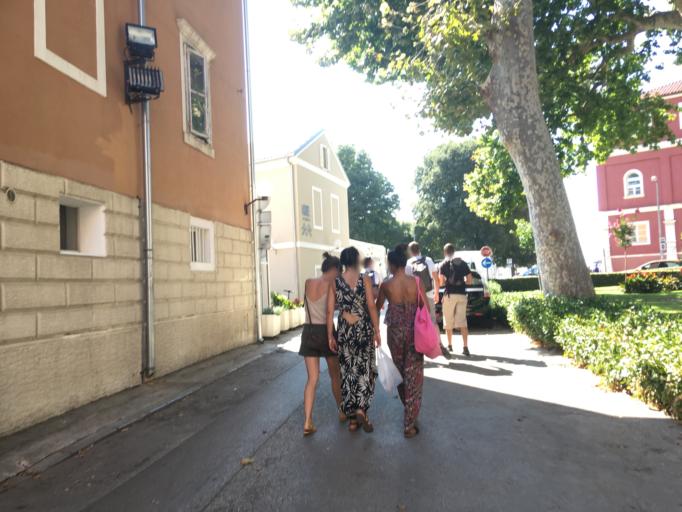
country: HR
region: Zadarska
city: Zadar
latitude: 44.1175
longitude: 15.2228
